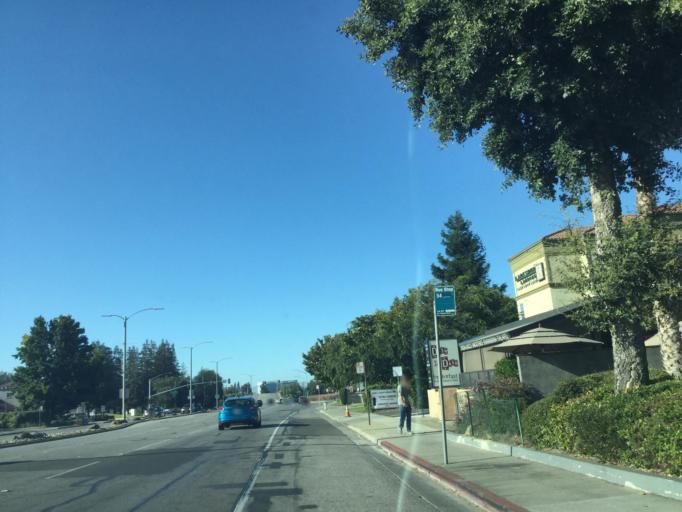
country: US
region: California
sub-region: Santa Clara County
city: Sunnyvale
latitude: 37.3941
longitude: -122.0291
